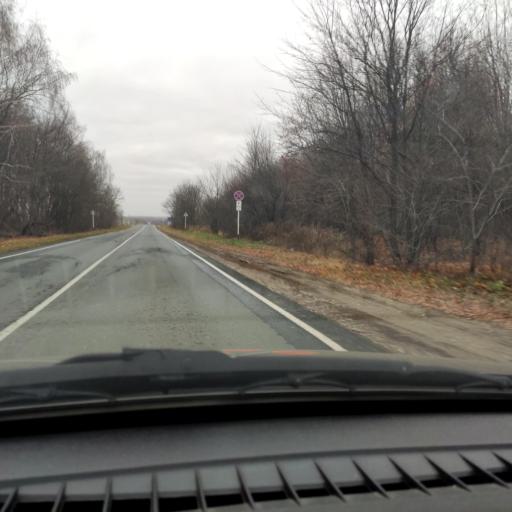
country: RU
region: Samara
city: Zhigulevsk
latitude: 53.3398
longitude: 49.4882
